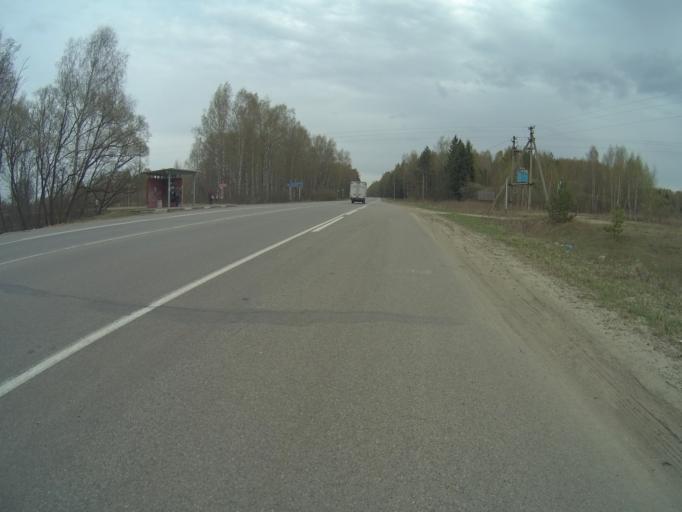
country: RU
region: Vladimir
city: Golovino
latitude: 55.9447
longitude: 40.5837
